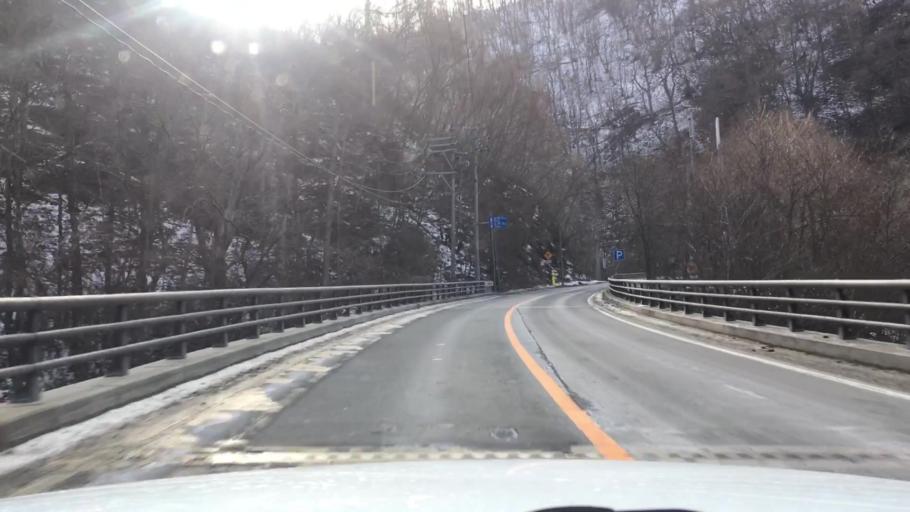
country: JP
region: Iwate
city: Tono
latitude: 39.6343
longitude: 141.5358
